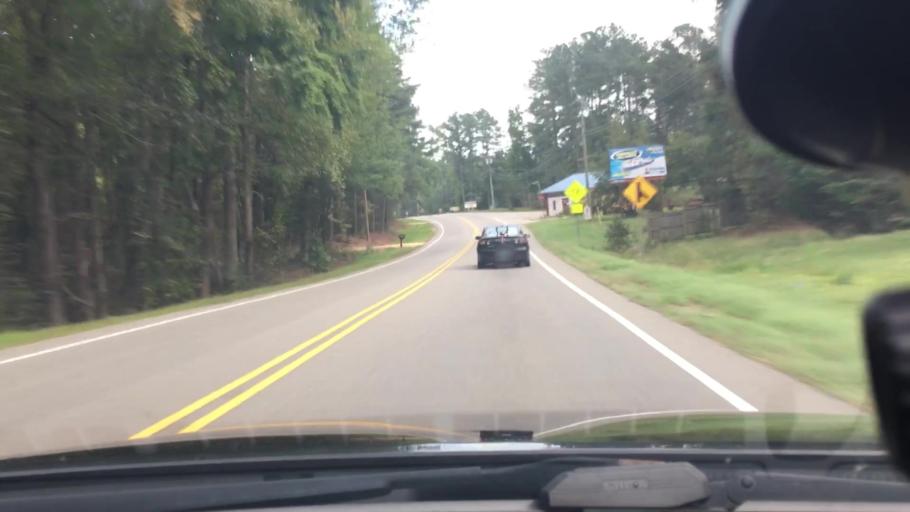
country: US
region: North Carolina
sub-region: Moore County
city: Carthage
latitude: 35.3580
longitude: -79.4332
